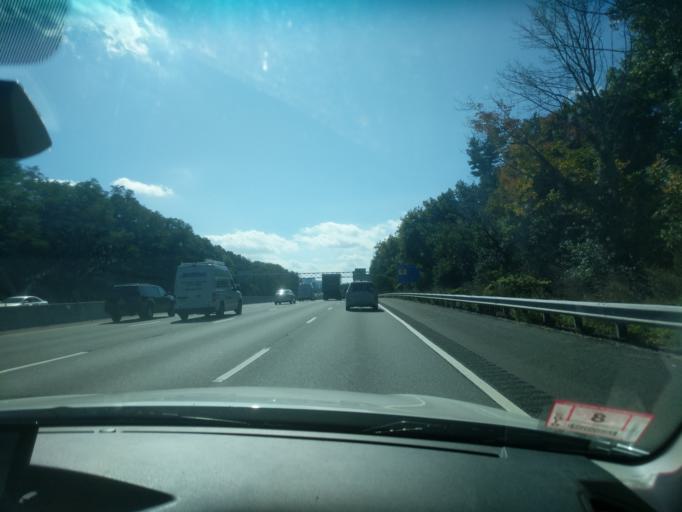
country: US
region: Massachusetts
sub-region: Middlesex County
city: Waltham
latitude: 42.4069
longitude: -71.2589
